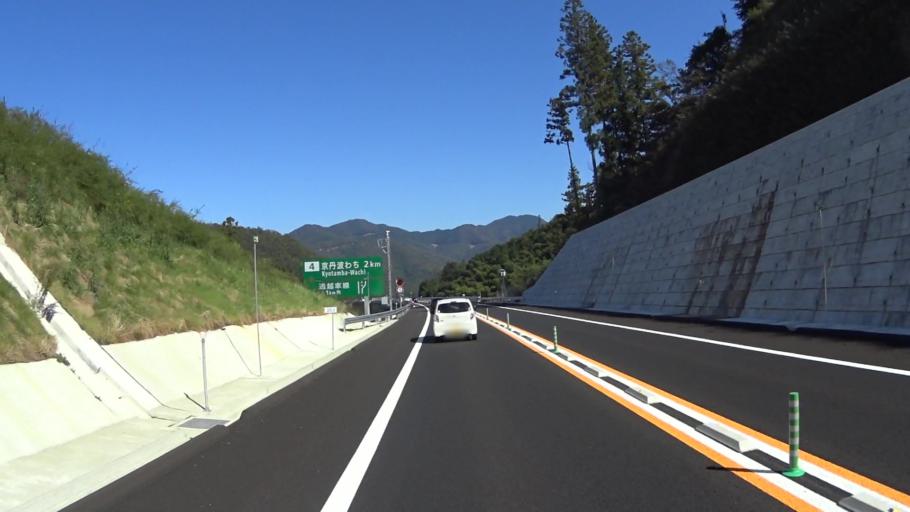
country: JP
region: Kyoto
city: Ayabe
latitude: 35.2613
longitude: 135.3444
